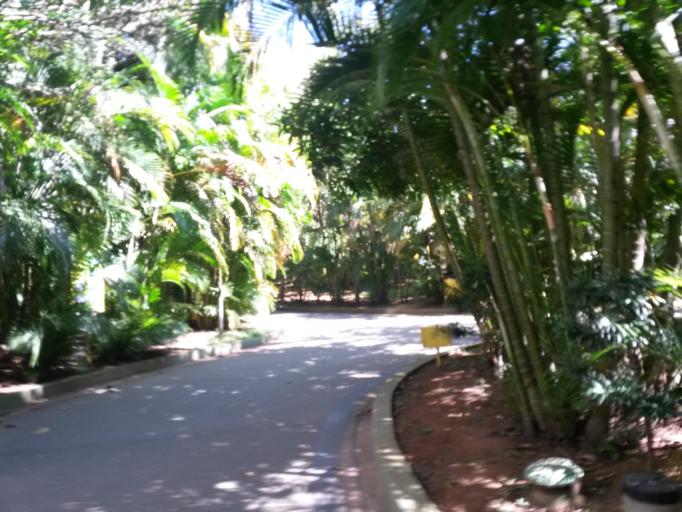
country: BR
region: Sao Paulo
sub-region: Sao Bernardo Do Campo
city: Sao Bernardo do Campo
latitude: -23.6807
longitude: -46.5587
